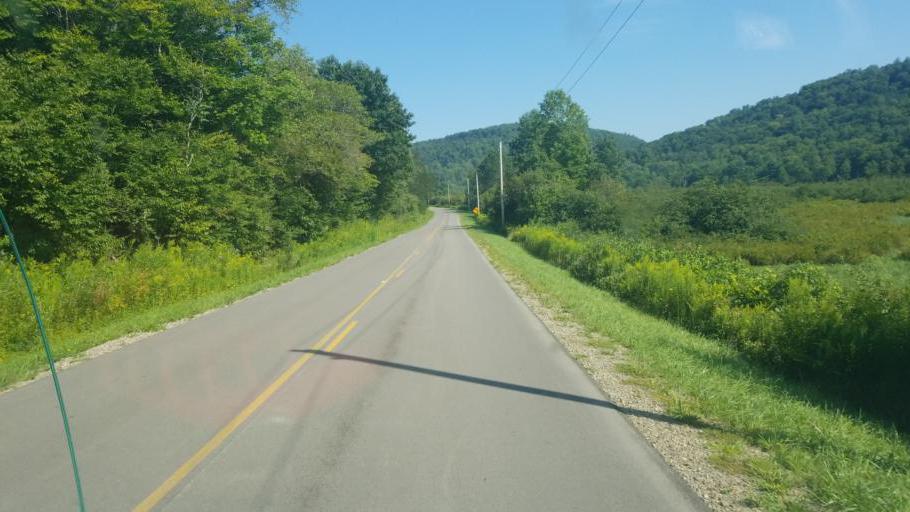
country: US
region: New York
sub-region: Allegany County
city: Bolivar
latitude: 42.0112
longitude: -78.0467
